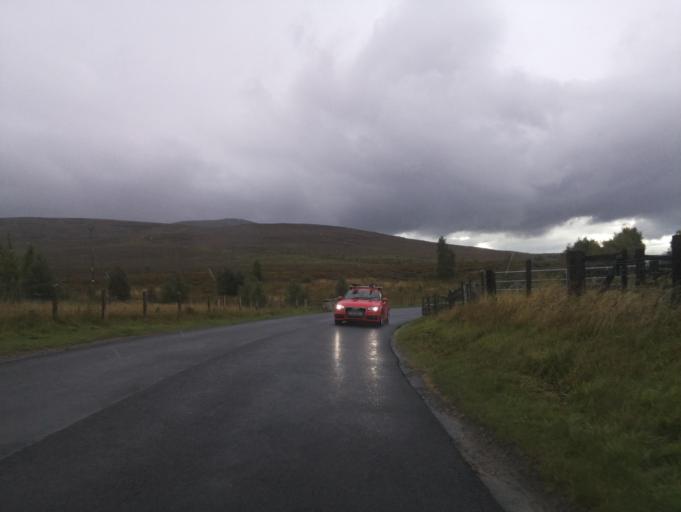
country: GB
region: Scotland
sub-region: Highland
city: Grantown on Spey
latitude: 57.2974
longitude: -3.5521
